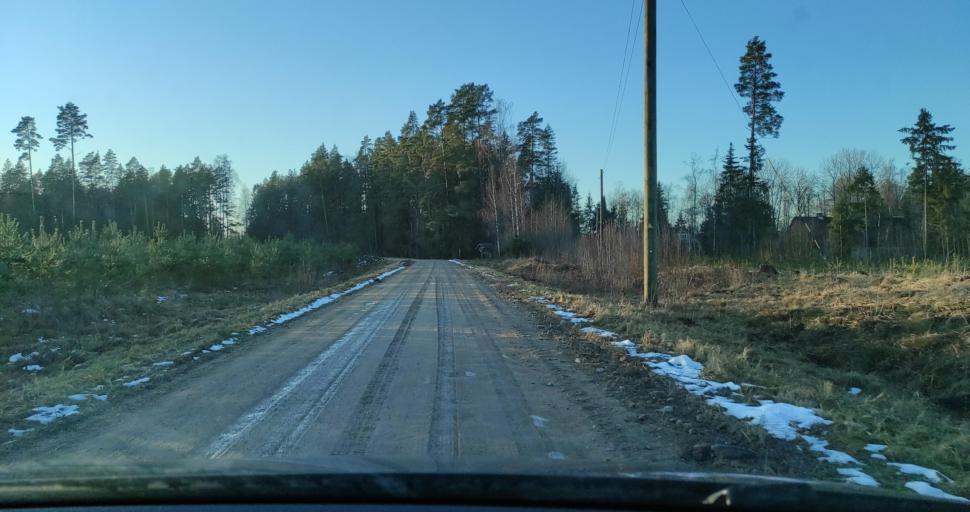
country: LV
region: Kuldigas Rajons
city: Kuldiga
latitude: 56.8774
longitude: 22.1445
